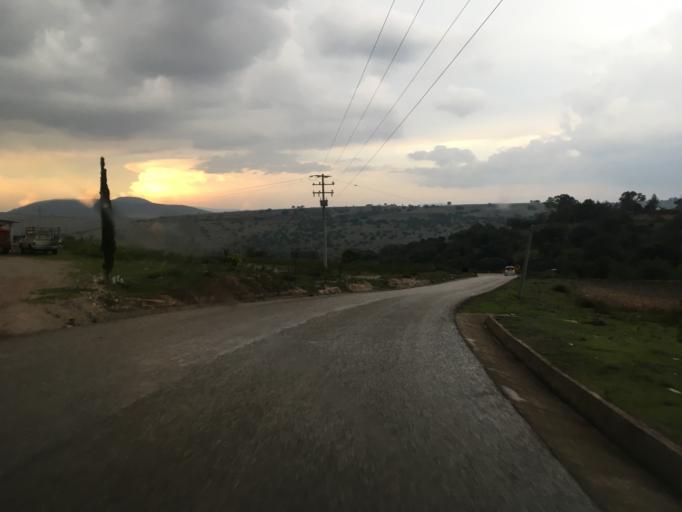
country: MX
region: Oaxaca
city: Santiago Tilantongo
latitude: 17.2880
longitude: -97.2797
